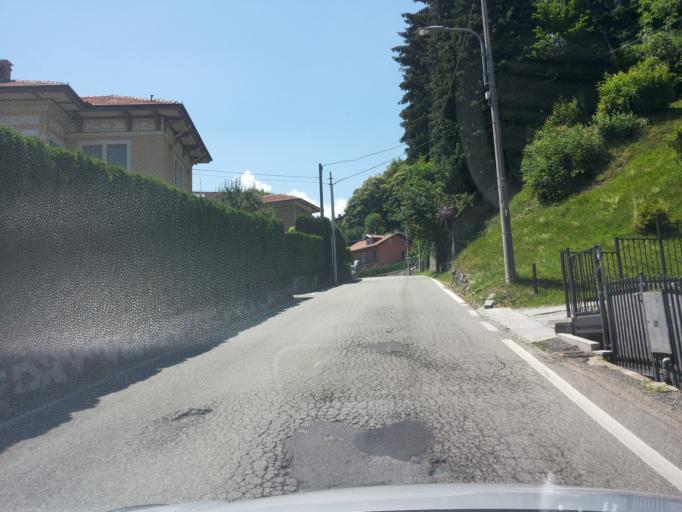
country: IT
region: Piedmont
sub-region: Provincia di Biella
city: Pralungo
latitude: 45.5976
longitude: 8.0222
